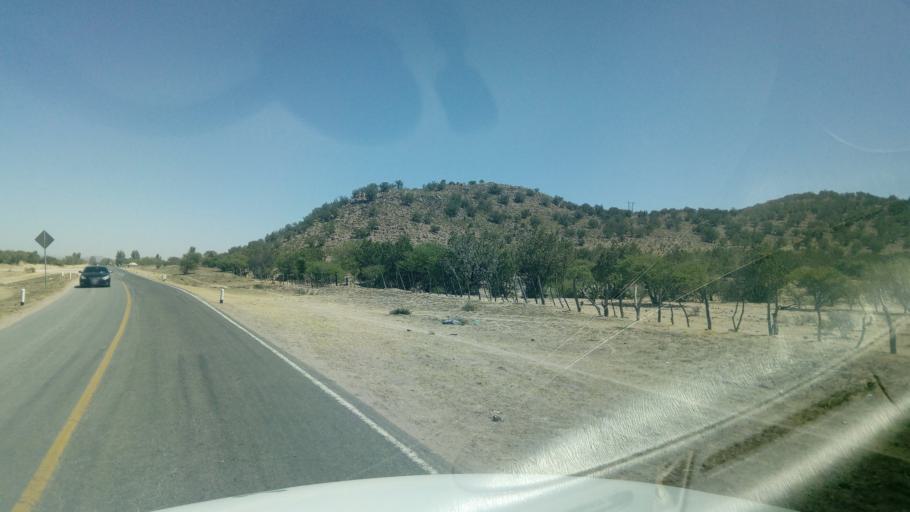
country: MX
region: Durango
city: Victoria de Durango
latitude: 24.1615
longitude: -104.7036
